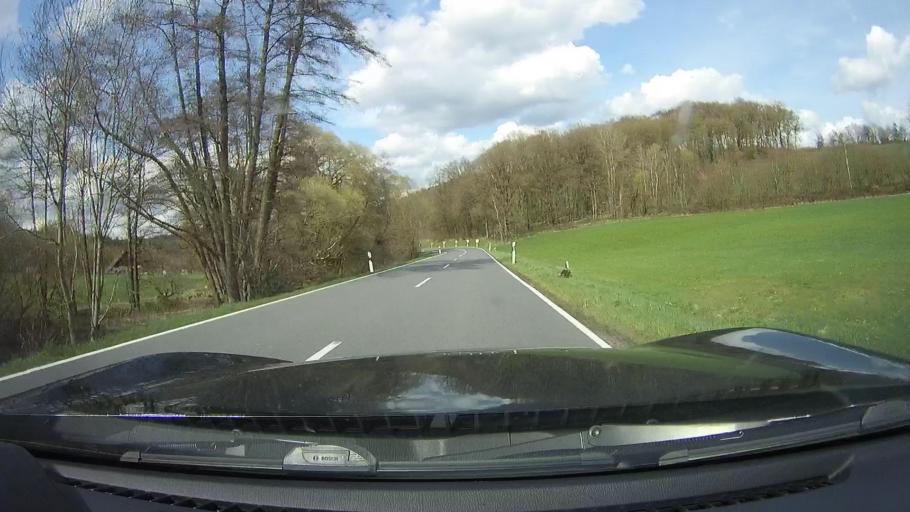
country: DE
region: Baden-Wuerttemberg
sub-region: Karlsruhe Region
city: Mudau
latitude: 49.5465
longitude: 9.2107
